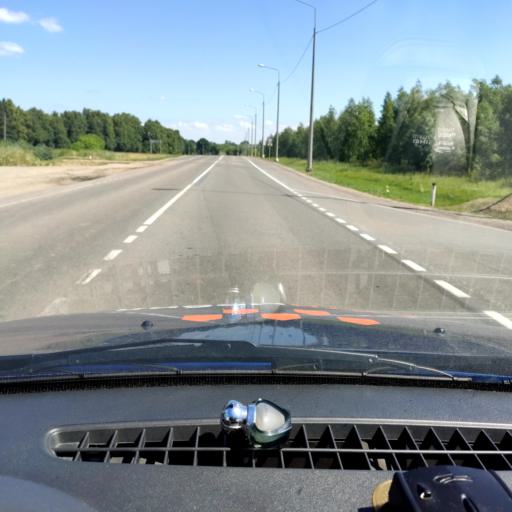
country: RU
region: Orjol
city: Pokrovskoye
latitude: 52.4957
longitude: 37.0590
